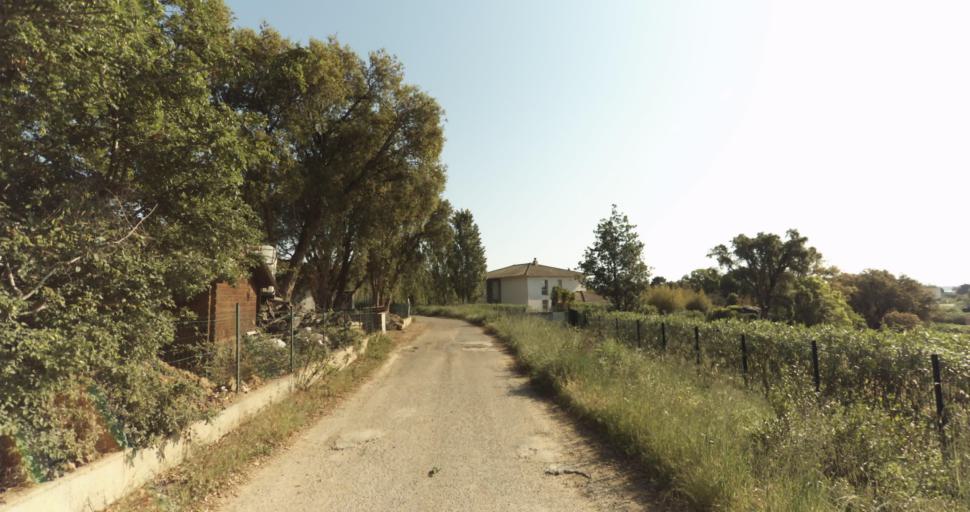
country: FR
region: Corsica
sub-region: Departement de la Haute-Corse
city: Biguglia
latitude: 42.6343
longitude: 9.4279
